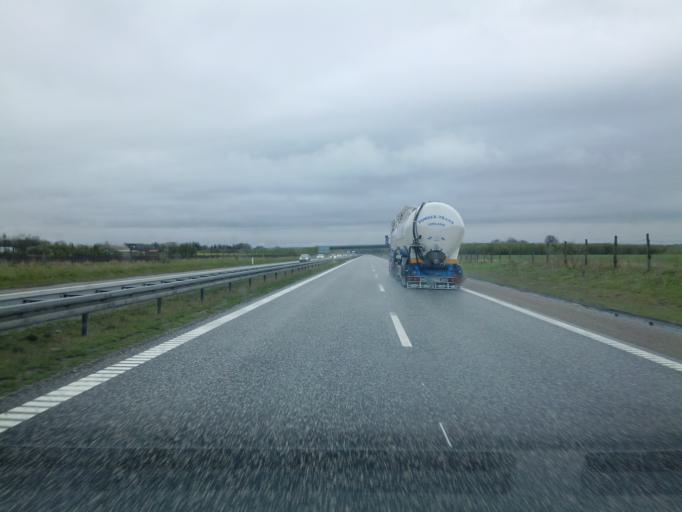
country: DK
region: North Denmark
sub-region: Bronderslev Kommune
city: Dronninglund
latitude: 57.2550
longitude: 10.3472
